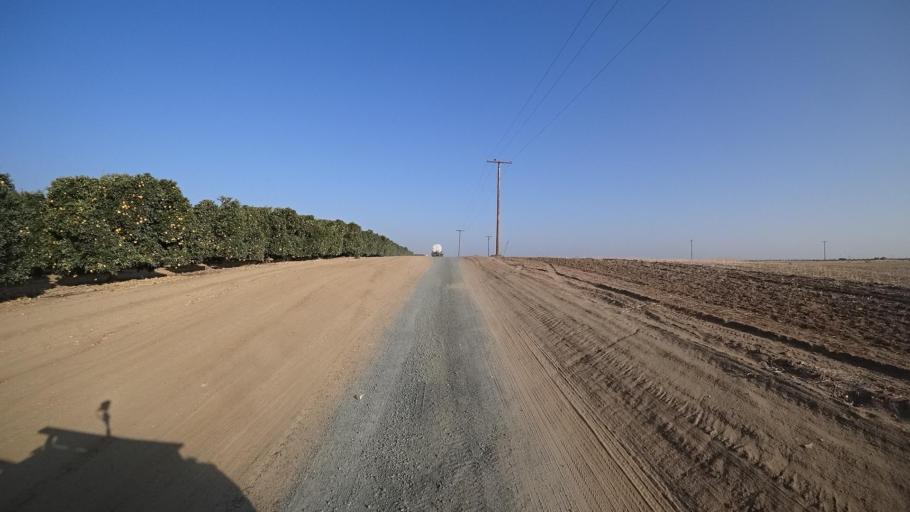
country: US
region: California
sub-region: Tulare County
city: Richgrove
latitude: 35.7750
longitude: -119.0807
